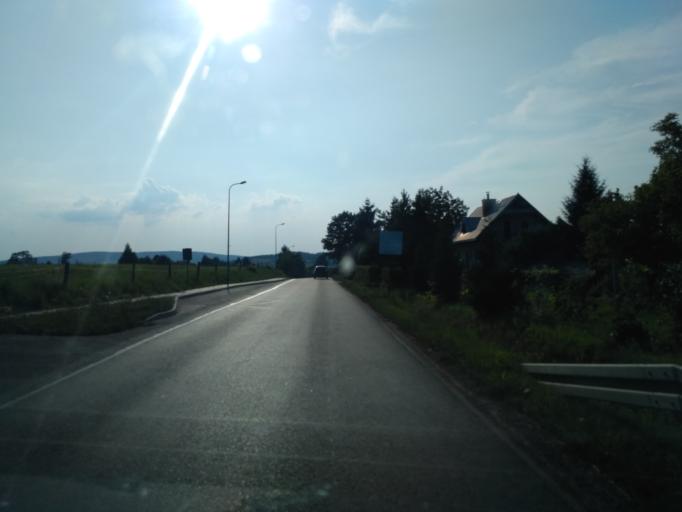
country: PL
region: Subcarpathian Voivodeship
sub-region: Powiat sanocki
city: Sanok
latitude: 49.5824
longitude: 22.1885
